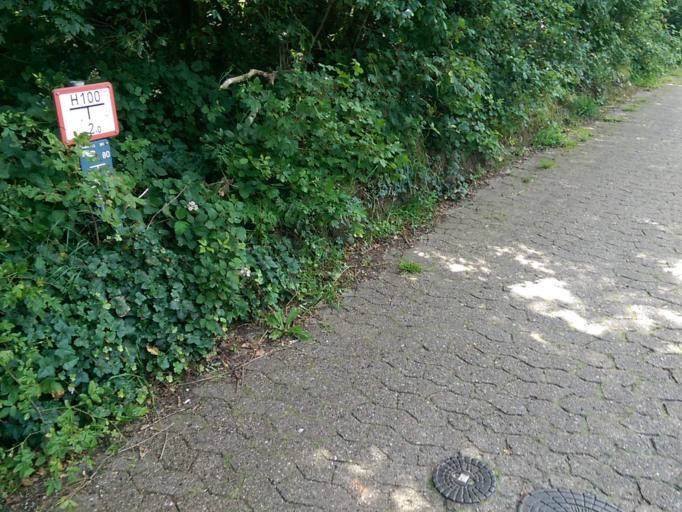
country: DE
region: Lower Saxony
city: Spiekeroog
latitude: 53.7710
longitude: 7.6997
